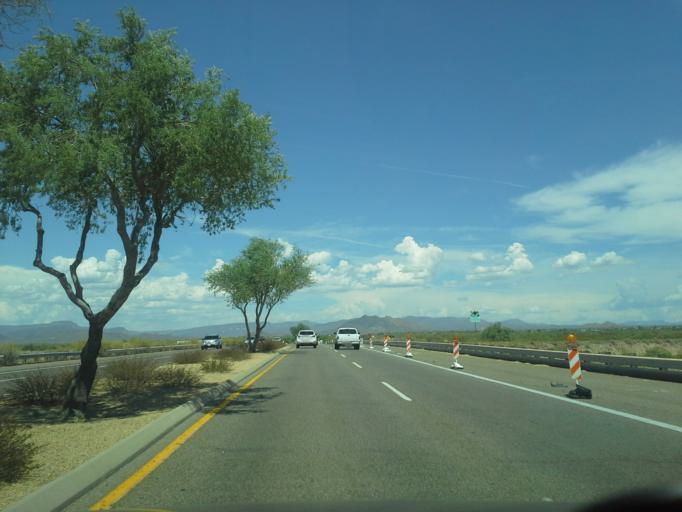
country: US
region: Arizona
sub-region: Maricopa County
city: Cave Creek
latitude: 33.7201
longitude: -112.0125
